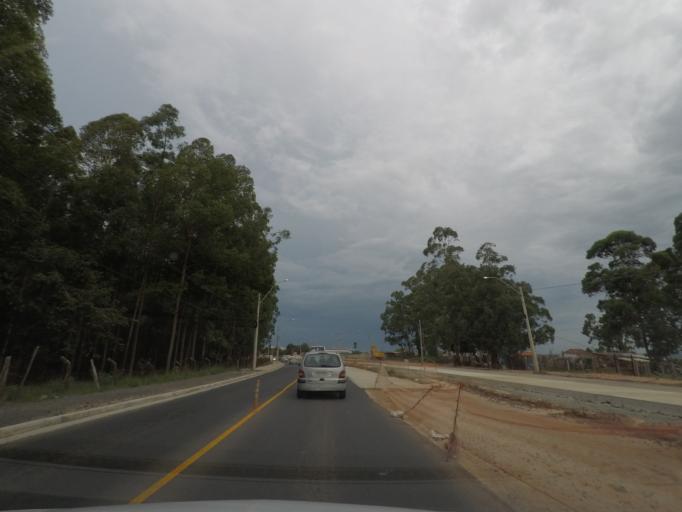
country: BR
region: Sao Paulo
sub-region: Hortolandia
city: Hortolandia
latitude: -22.9427
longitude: -47.1785
